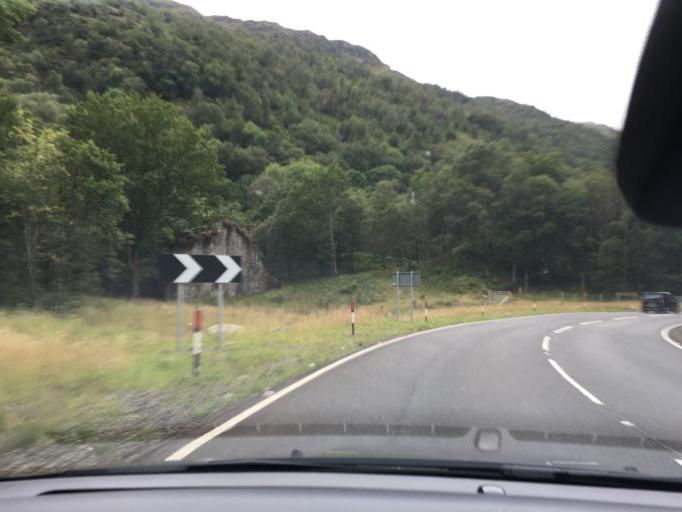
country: GB
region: Scotland
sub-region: Argyll and Bute
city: Garelochhead
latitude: 56.2860
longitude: -4.7061
